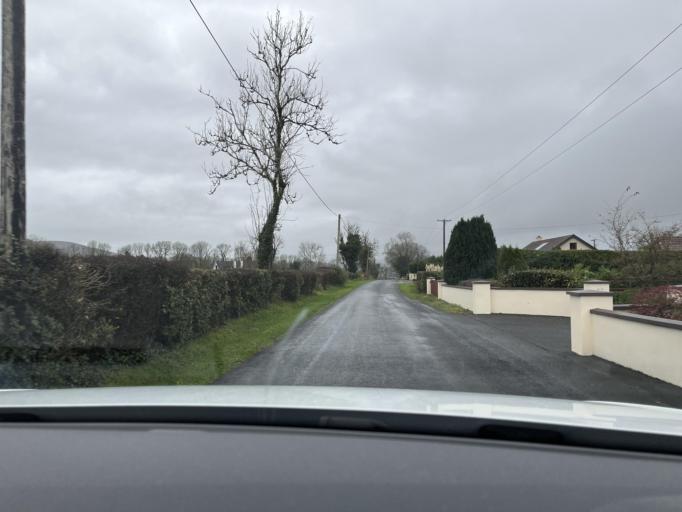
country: IE
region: Connaught
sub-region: County Leitrim
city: Manorhamilton
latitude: 54.2992
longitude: -8.1487
